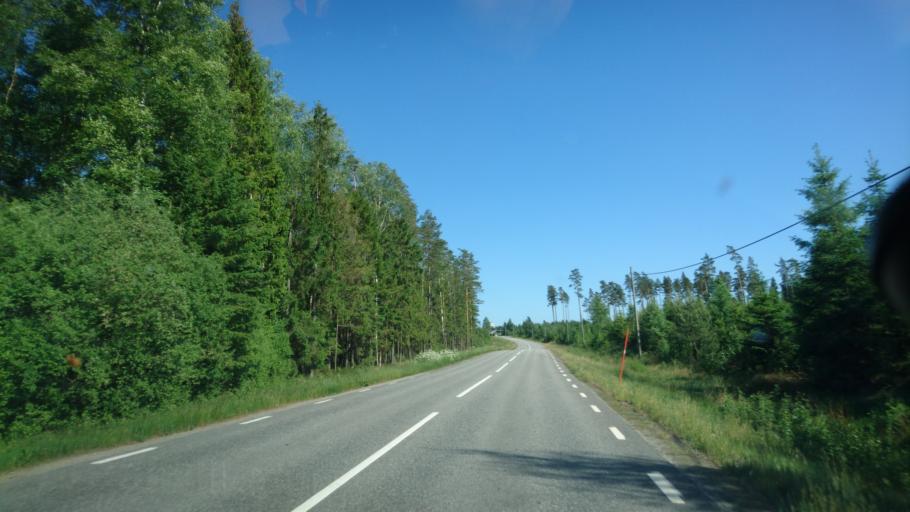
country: SE
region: Skane
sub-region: Osby Kommun
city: Lonsboda
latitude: 56.4137
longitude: 14.3004
